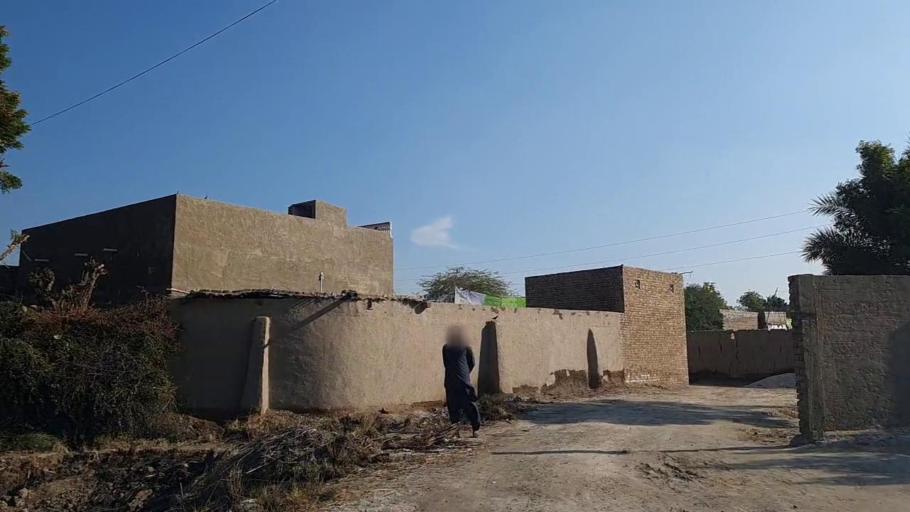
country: PK
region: Sindh
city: Bandhi
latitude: 26.5723
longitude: 68.3114
